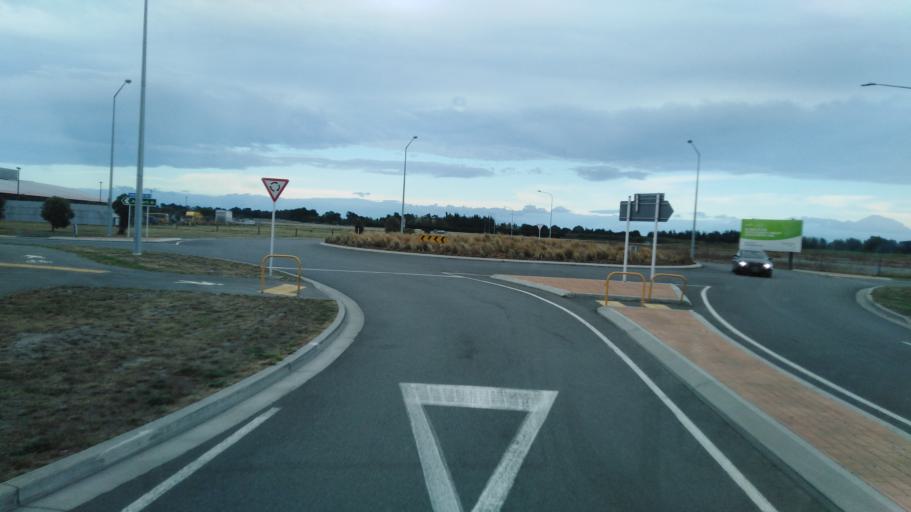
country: NZ
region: Canterbury
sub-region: Christchurch City
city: Christchurch
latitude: -43.4780
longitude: 172.5539
